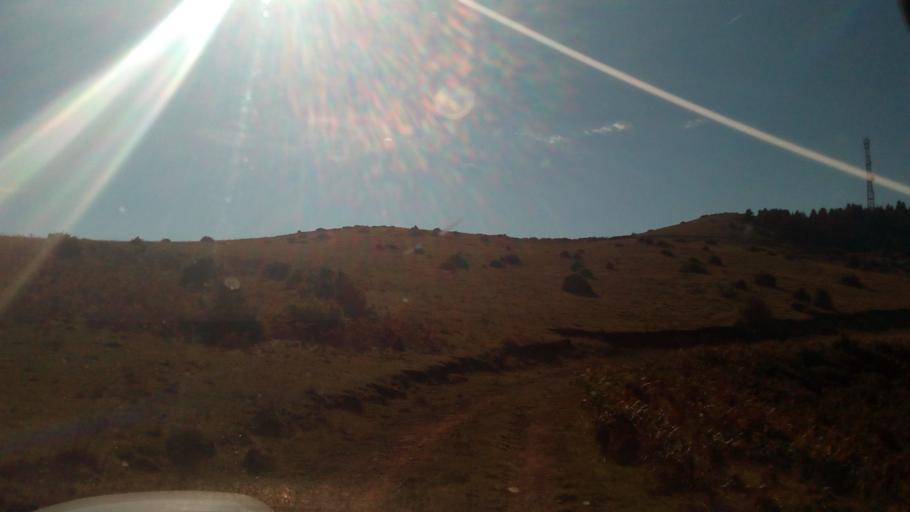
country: GR
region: Central Greece
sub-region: Nomos Fokidos
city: Lidoriki
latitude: 38.6072
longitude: 21.9655
